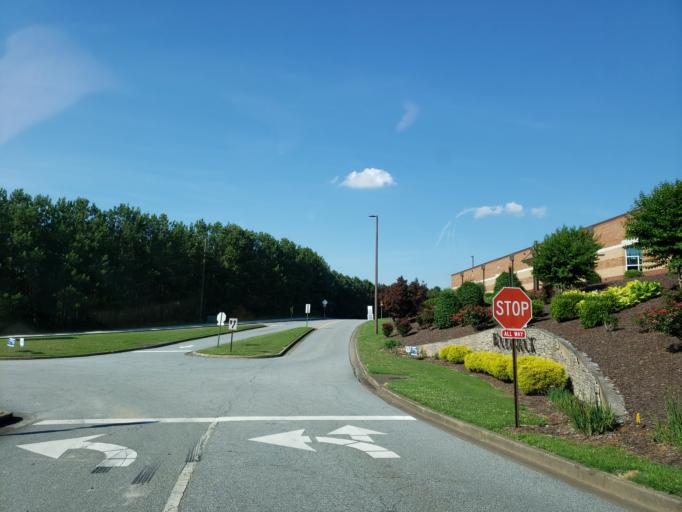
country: US
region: Georgia
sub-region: Cherokee County
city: Woodstock
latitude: 34.1016
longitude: -84.5432
